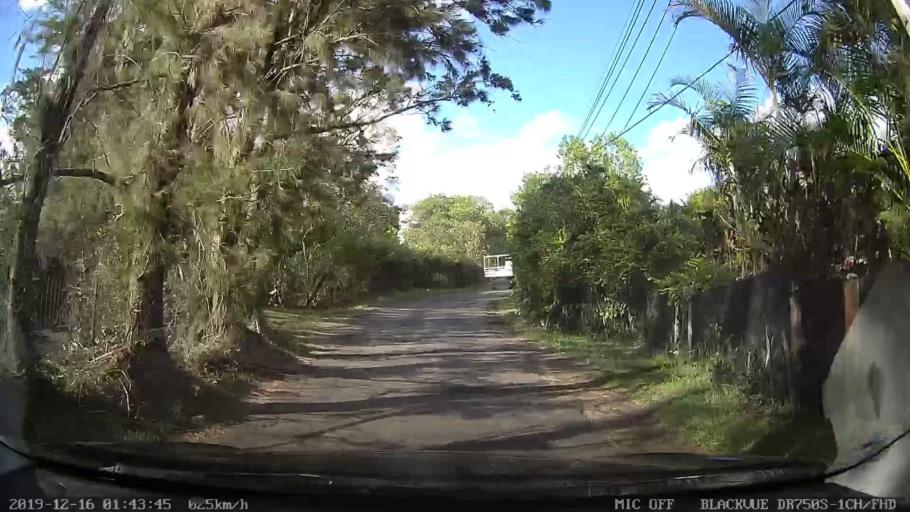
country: RE
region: Reunion
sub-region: Reunion
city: Le Tampon
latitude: -21.2506
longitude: 55.5133
